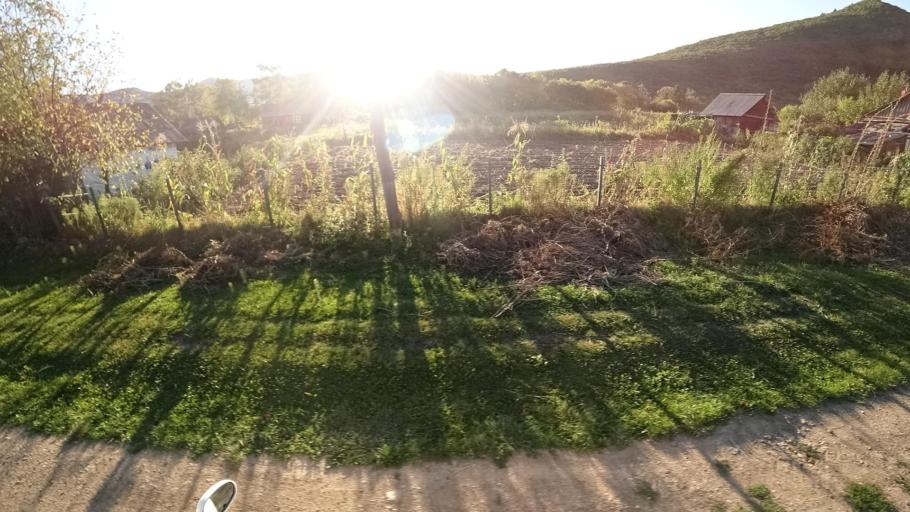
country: RU
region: Primorskiy
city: Kirovskiy
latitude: 44.8324
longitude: 133.5755
